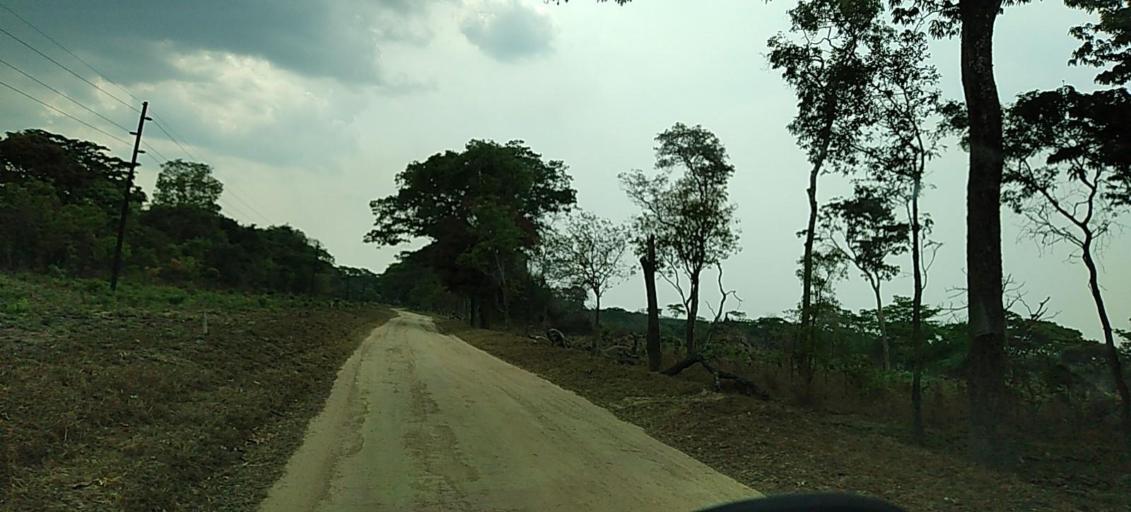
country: ZM
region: North-Western
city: Solwezi
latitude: -12.7717
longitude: 26.4672
